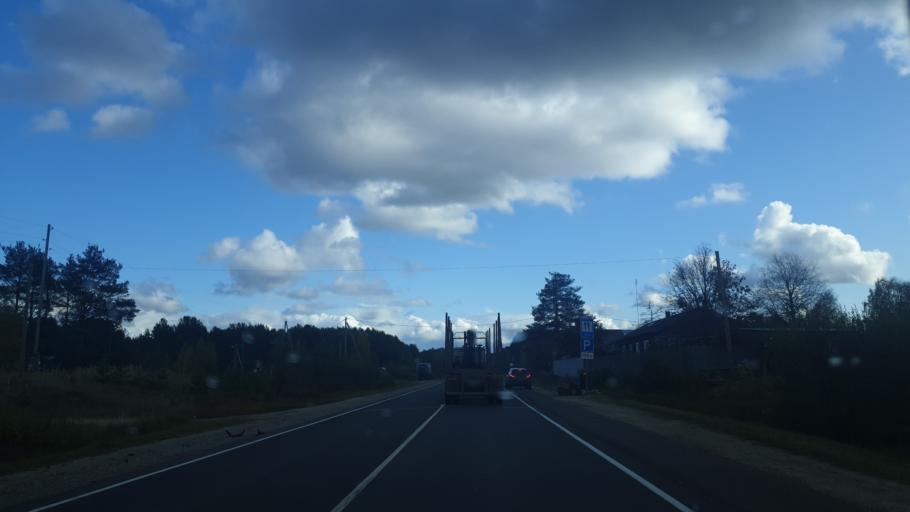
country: RU
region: Komi Republic
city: Vizinga
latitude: 60.4631
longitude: 49.6656
